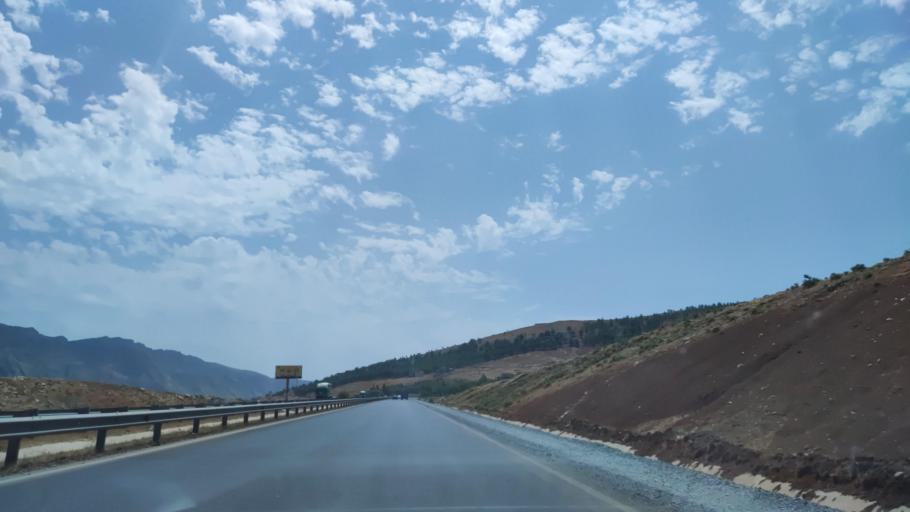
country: IQ
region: Arbil
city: Shaqlawah
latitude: 36.4957
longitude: 44.3657
